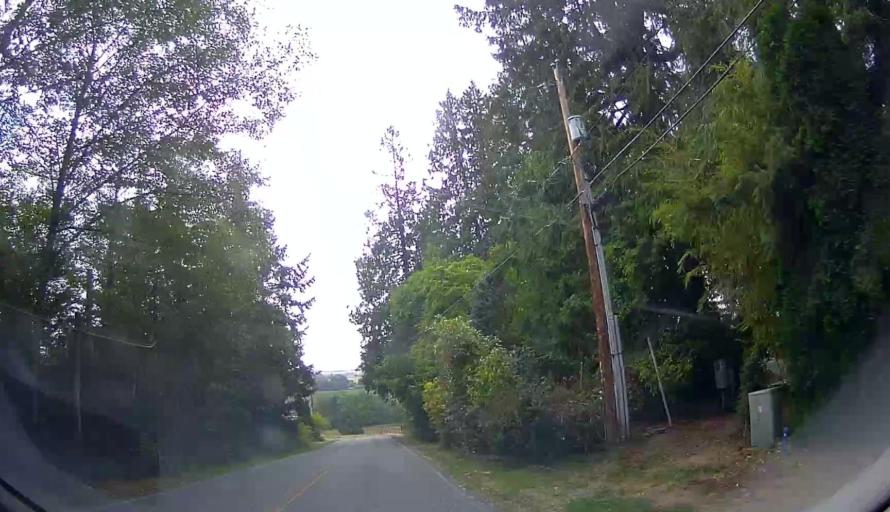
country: US
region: Washington
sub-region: Skagit County
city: Burlington
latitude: 48.5812
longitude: -122.3992
